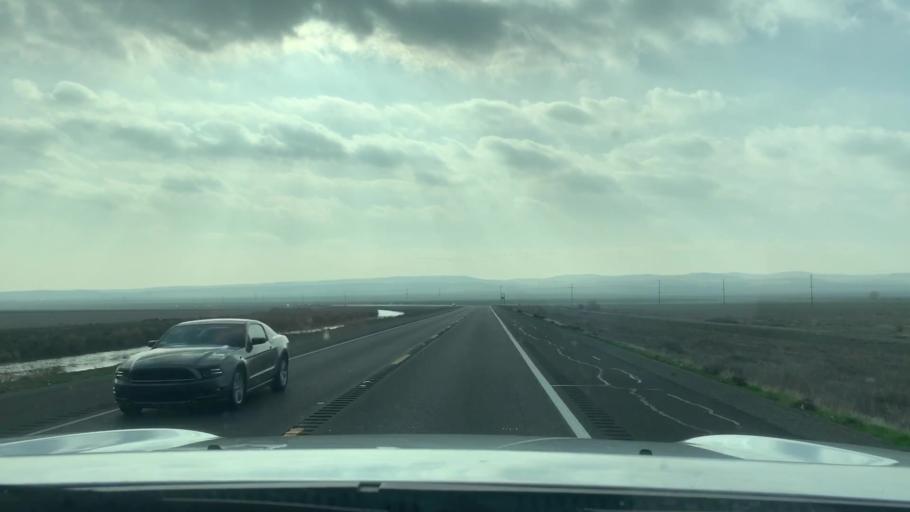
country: US
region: California
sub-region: Kings County
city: Kettleman City
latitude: 36.0424
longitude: -119.9535
